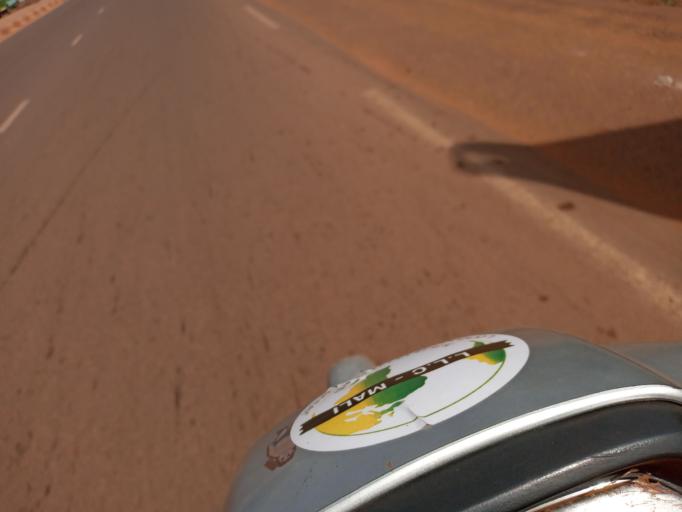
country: ML
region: Bamako
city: Bamako
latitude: 12.5619
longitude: -7.9809
